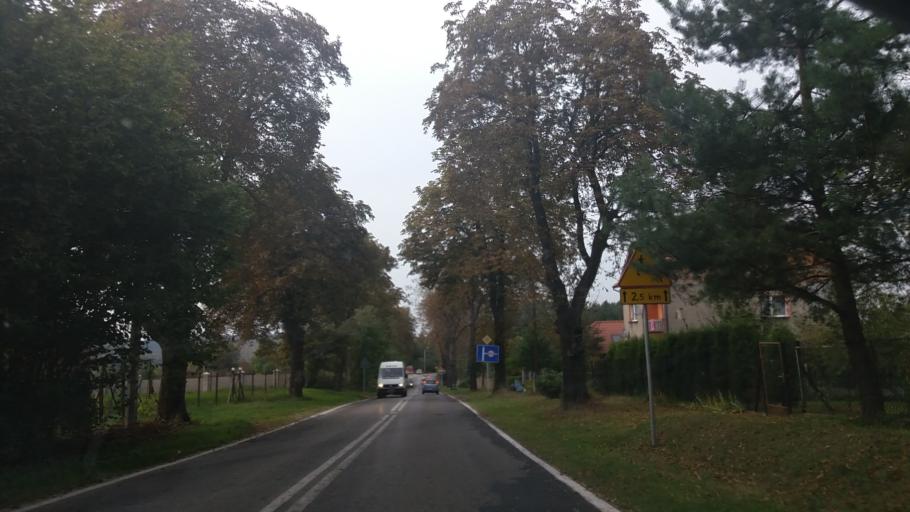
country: PL
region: Lesser Poland Voivodeship
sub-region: Powiat chrzanowski
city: Plaza
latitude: 50.1041
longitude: 19.4489
